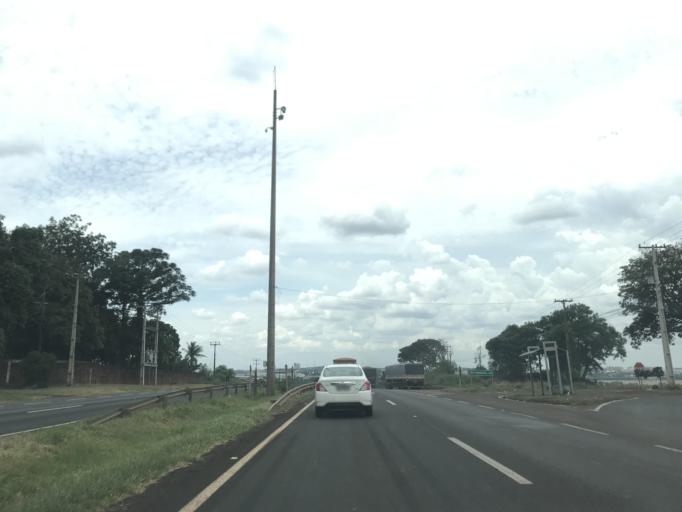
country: BR
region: Parana
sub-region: Maringa
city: Maringa
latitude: -23.4000
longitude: -52.0009
